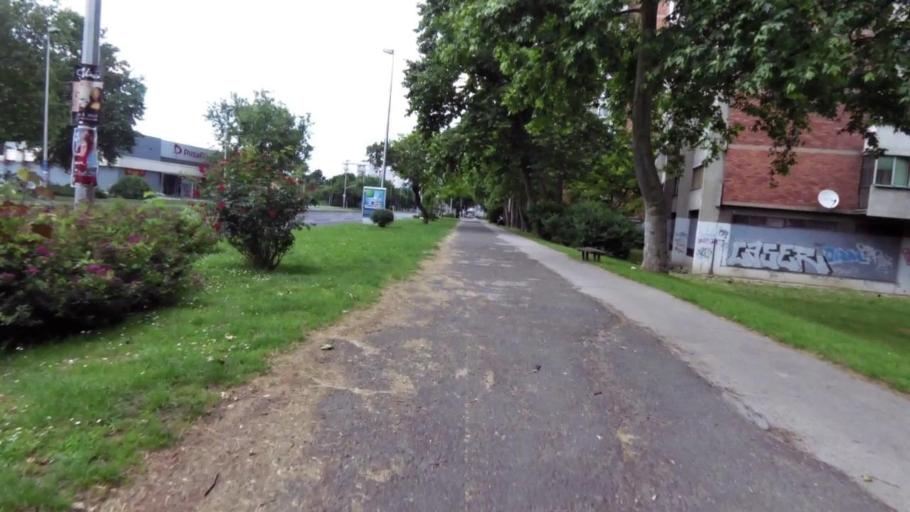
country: HR
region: Grad Zagreb
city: Novi Zagreb
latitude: 45.7902
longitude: 15.9452
